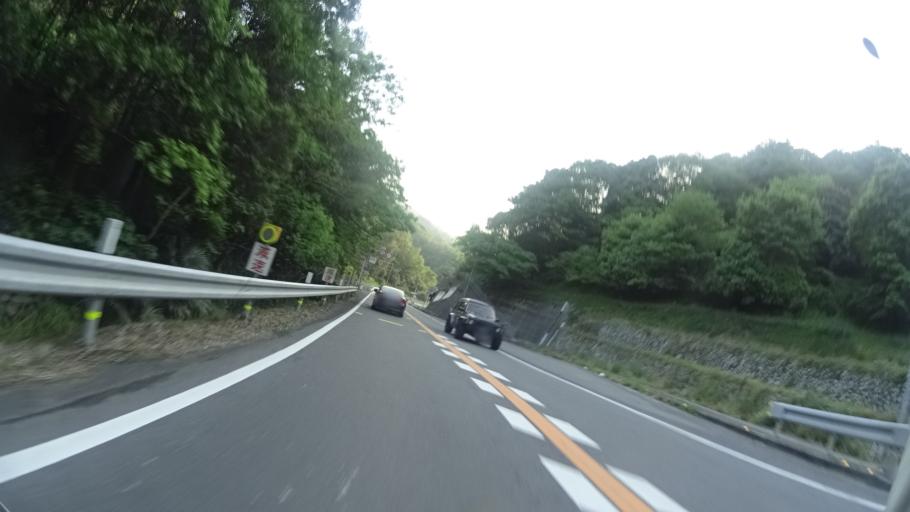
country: JP
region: Ehime
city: Kawanoecho
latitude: 33.9911
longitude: 133.6399
